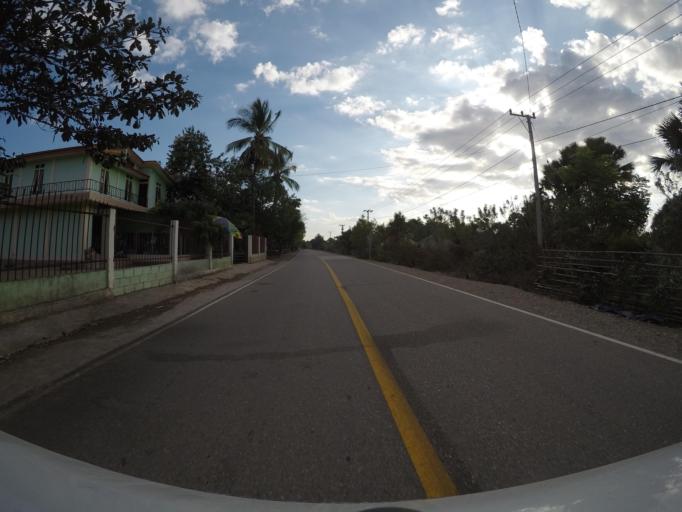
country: TL
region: Bobonaro
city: Maliana
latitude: -8.8810
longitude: 125.0314
